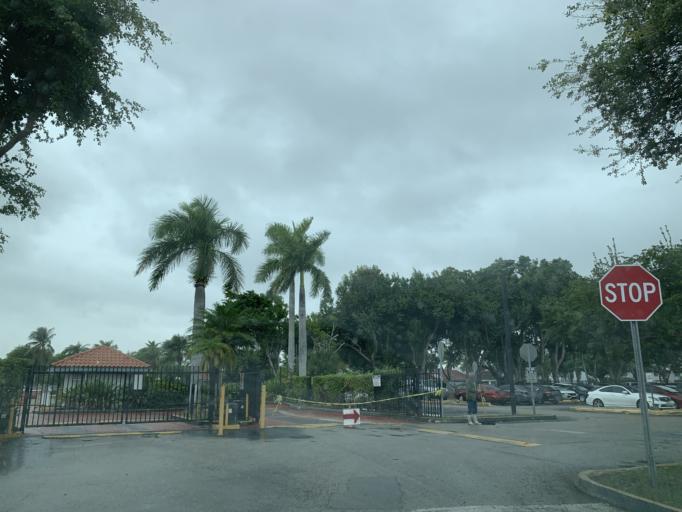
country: US
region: Florida
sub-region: Miami-Dade County
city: Kendall West
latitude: 25.6898
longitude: -80.4392
